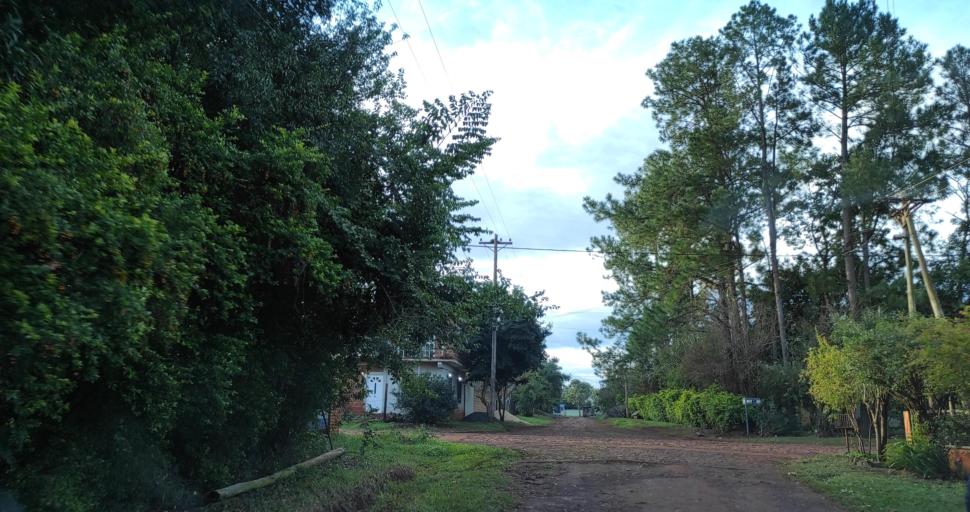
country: AR
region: Misiones
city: Garupa
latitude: -27.4808
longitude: -55.8596
